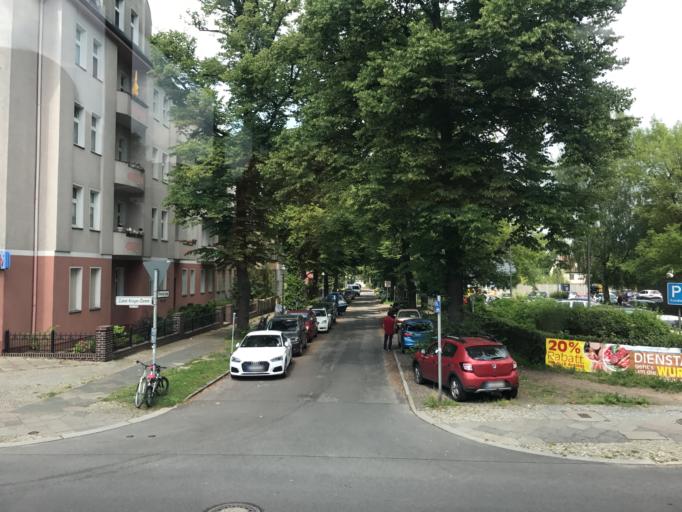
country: DE
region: Berlin
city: Waidmannslust
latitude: 52.6089
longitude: 13.3280
